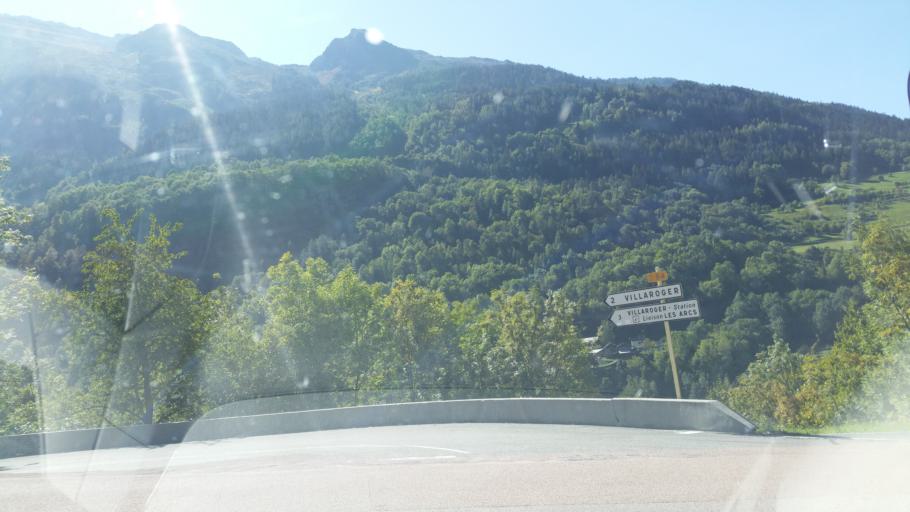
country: FR
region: Rhone-Alpes
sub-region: Departement de la Savoie
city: Seez
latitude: 45.5888
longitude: 6.8836
